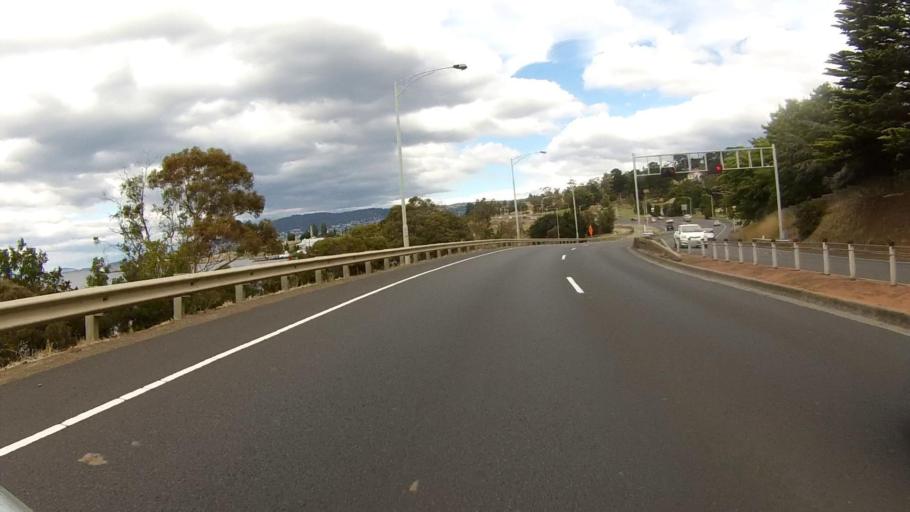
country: AU
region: Tasmania
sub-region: Hobart
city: Hobart
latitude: -42.8687
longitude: 147.3356
